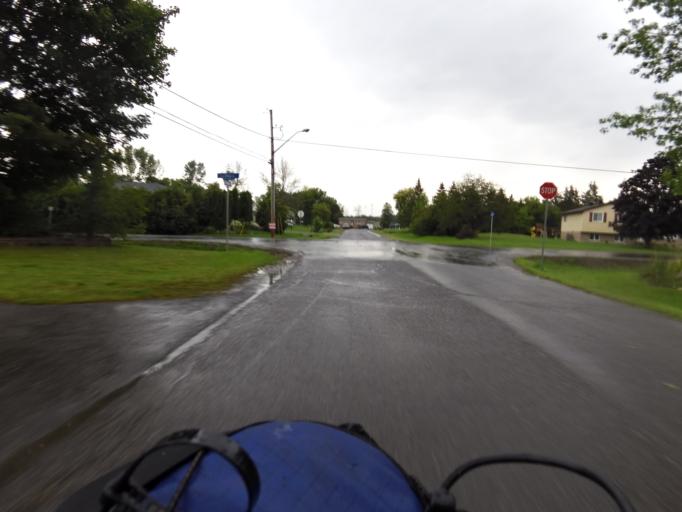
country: CA
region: Ontario
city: Ottawa
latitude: 45.2367
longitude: -75.4761
